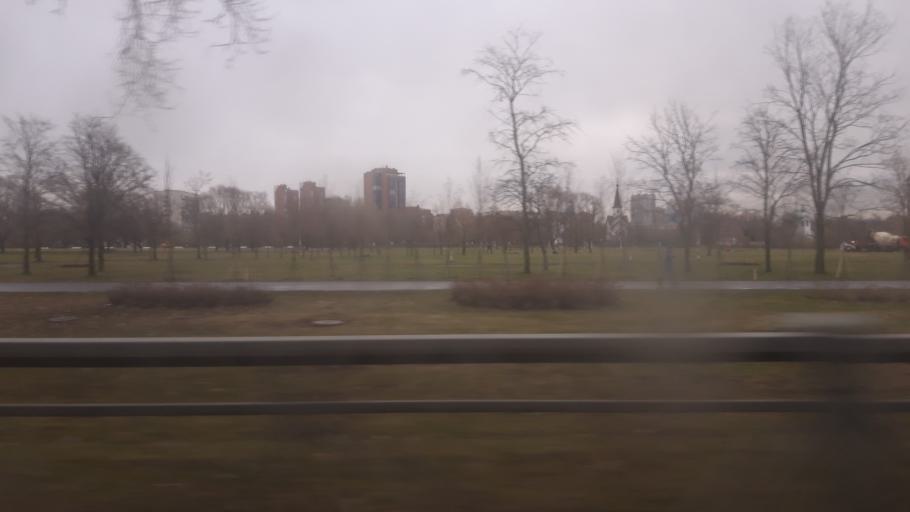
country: RU
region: St.-Petersburg
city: Kupchino
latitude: 59.8373
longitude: 30.3226
